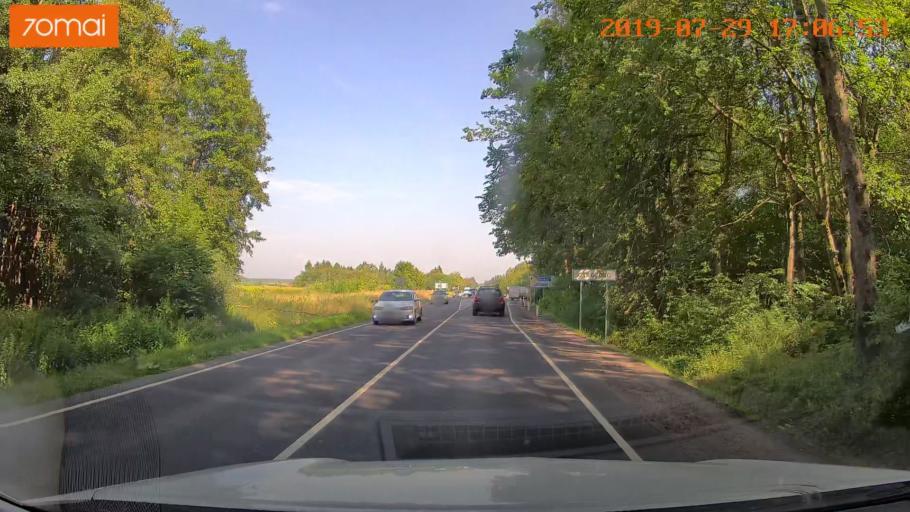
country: RU
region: Kaliningrad
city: Vzmorye
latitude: 54.8189
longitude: 20.3141
